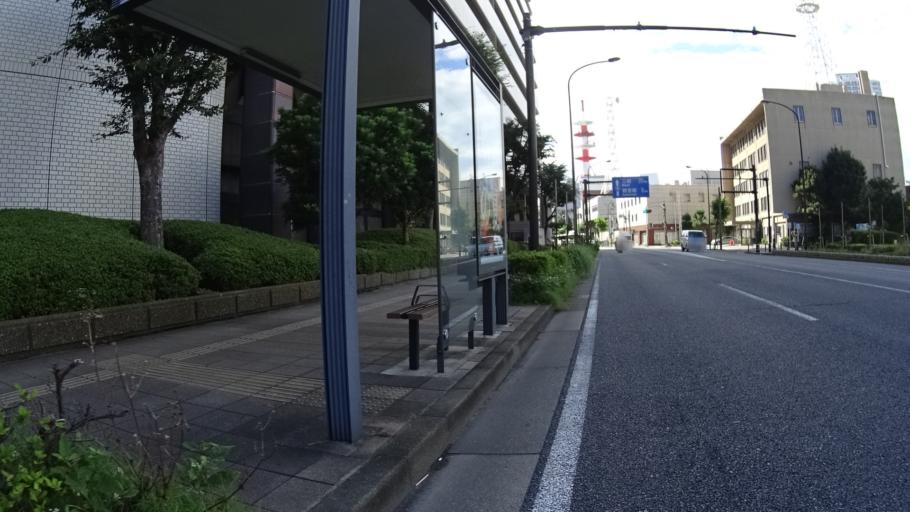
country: JP
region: Kanagawa
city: Yokosuka
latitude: 35.2815
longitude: 139.6717
